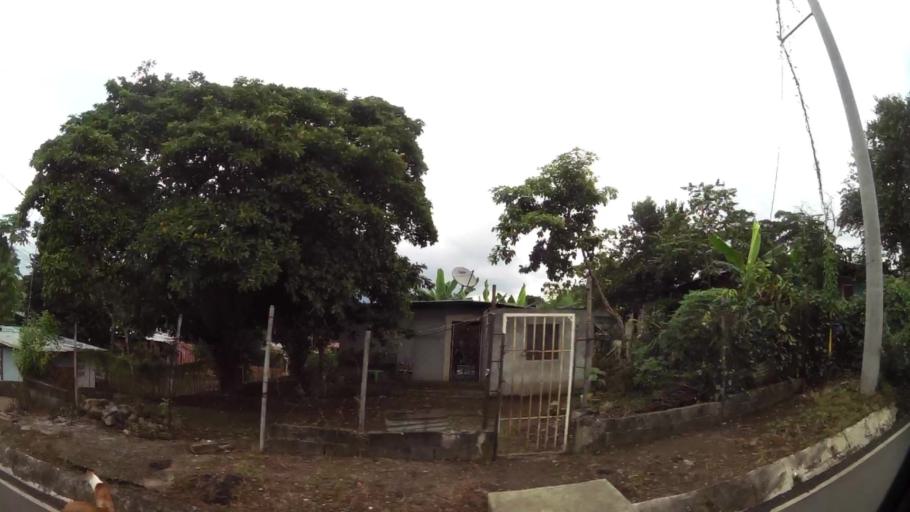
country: PA
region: Panama
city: Cabra Numero Uno
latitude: 9.1108
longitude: -79.3614
